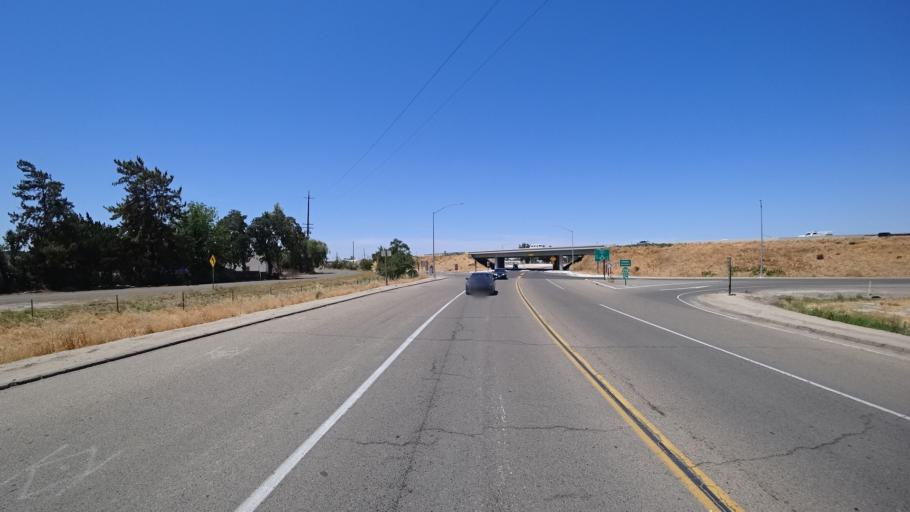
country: US
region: California
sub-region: Kings County
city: Armona
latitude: 36.3136
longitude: -119.6913
